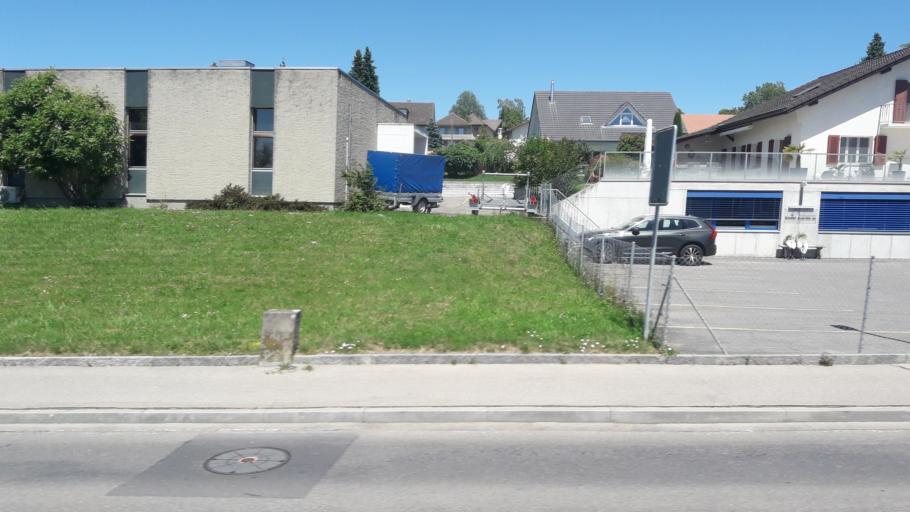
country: CH
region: Bern
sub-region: Seeland District
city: Ins
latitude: 47.0069
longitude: 7.1110
